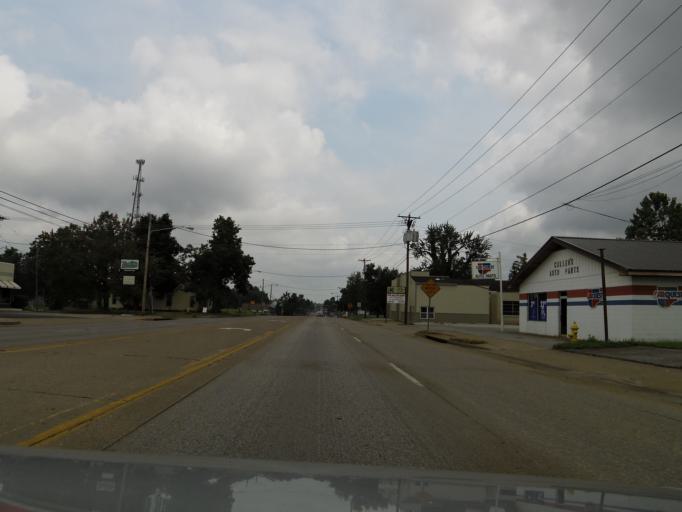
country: US
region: Kentucky
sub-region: Hopkins County
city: Madisonville
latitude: 37.3193
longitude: -87.5002
